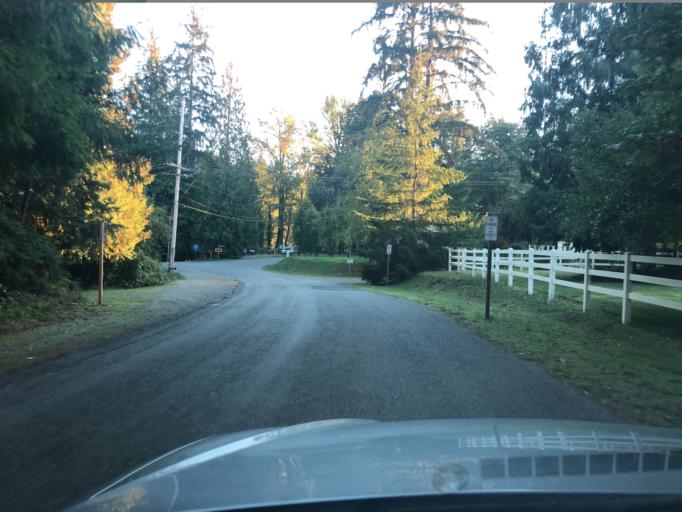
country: US
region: Washington
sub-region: King County
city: Snoqualmie
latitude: 47.5524
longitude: -121.8443
